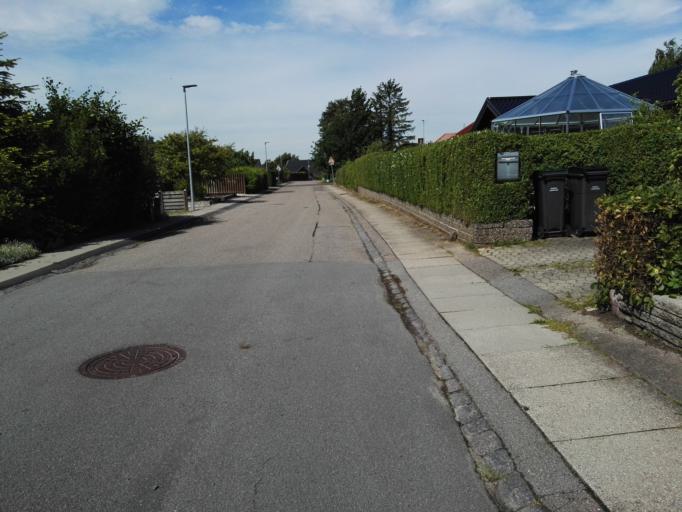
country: DK
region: Capital Region
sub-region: Egedal Kommune
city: Olstykke
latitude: 55.7935
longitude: 12.1400
